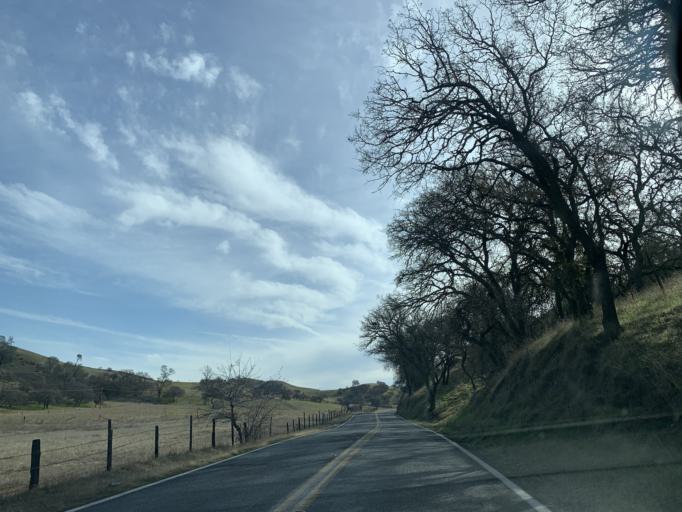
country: US
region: California
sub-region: Monterey County
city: Soledad
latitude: 36.5103
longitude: -121.1147
